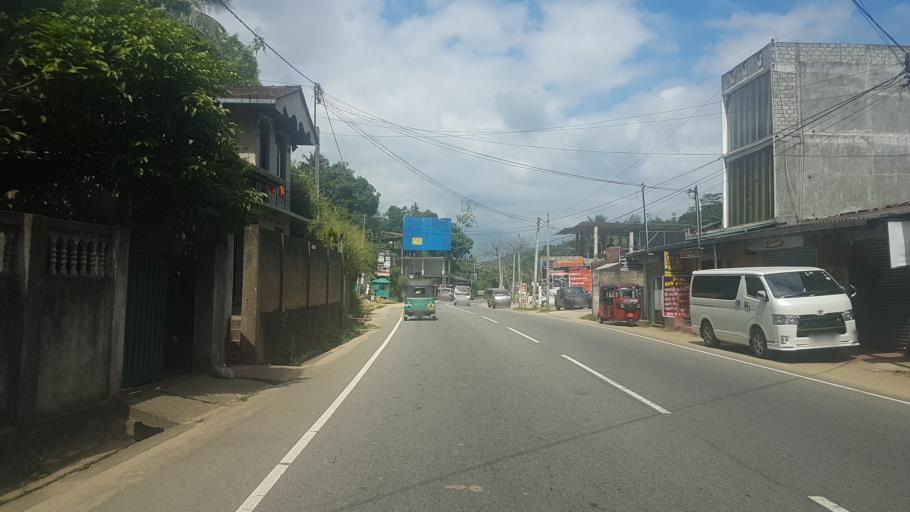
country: LK
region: Central
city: Gampola
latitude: 7.2028
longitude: 80.5993
